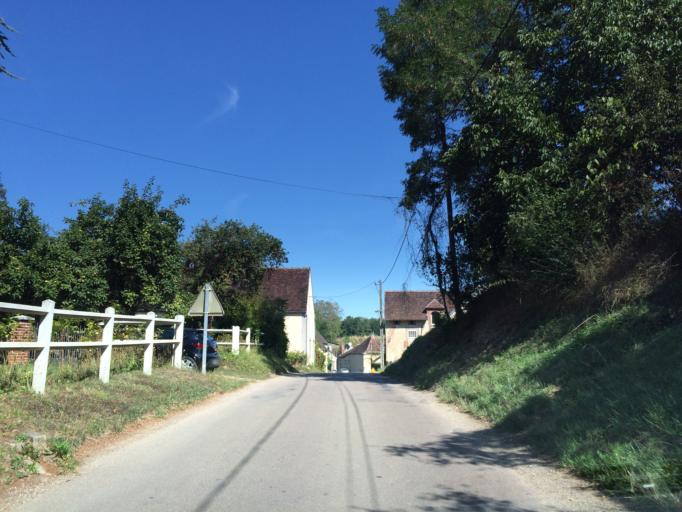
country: FR
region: Bourgogne
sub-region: Departement de l'Yonne
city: Fleury-la-Vallee
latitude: 47.8466
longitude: 3.4001
